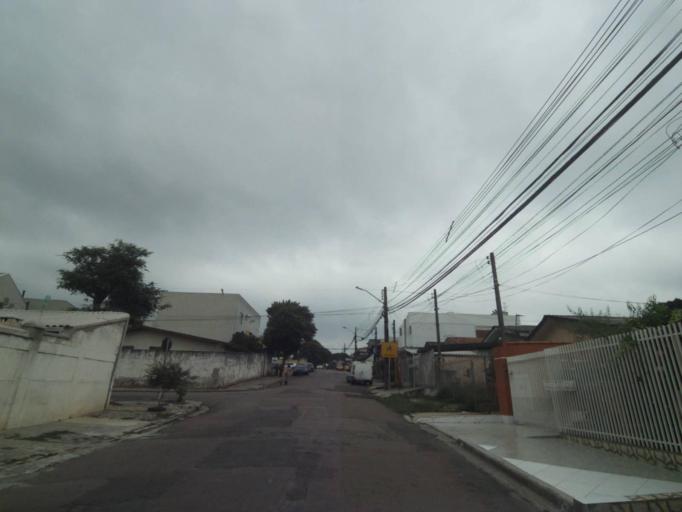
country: BR
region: Parana
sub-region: Curitiba
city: Curitiba
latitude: -25.4848
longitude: -49.3491
